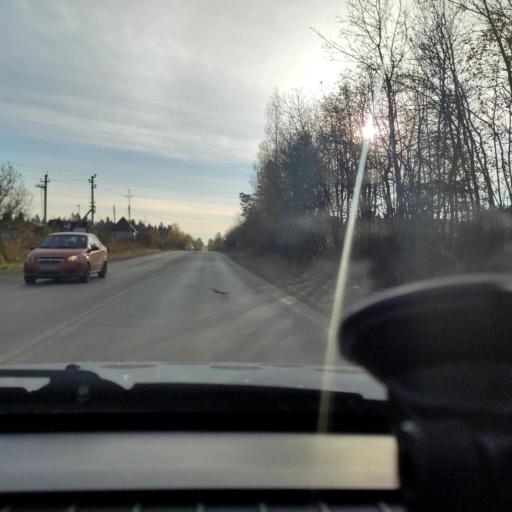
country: RU
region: Perm
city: Ferma
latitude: 57.9484
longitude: 56.4022
